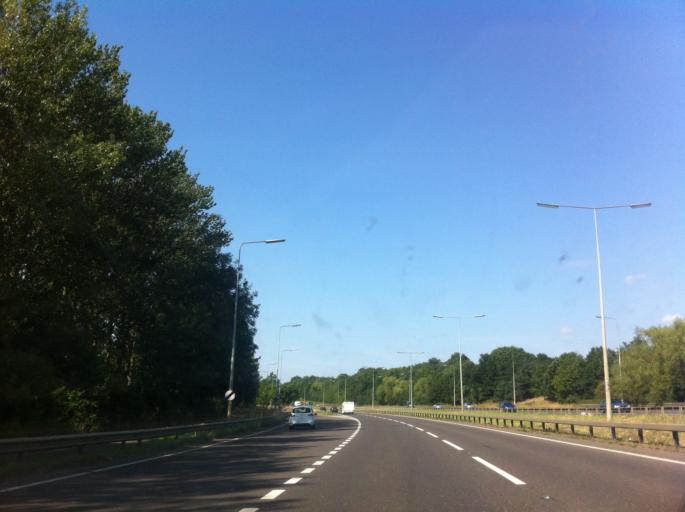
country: GB
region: England
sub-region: Northamptonshire
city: Northampton
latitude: 52.2467
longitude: -0.8271
